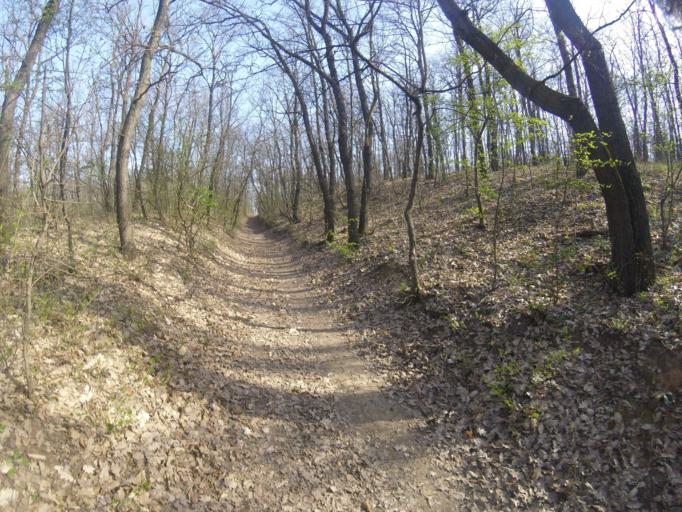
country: HU
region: Komarom-Esztergom
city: Piliscsev
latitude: 47.6648
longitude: 18.8003
